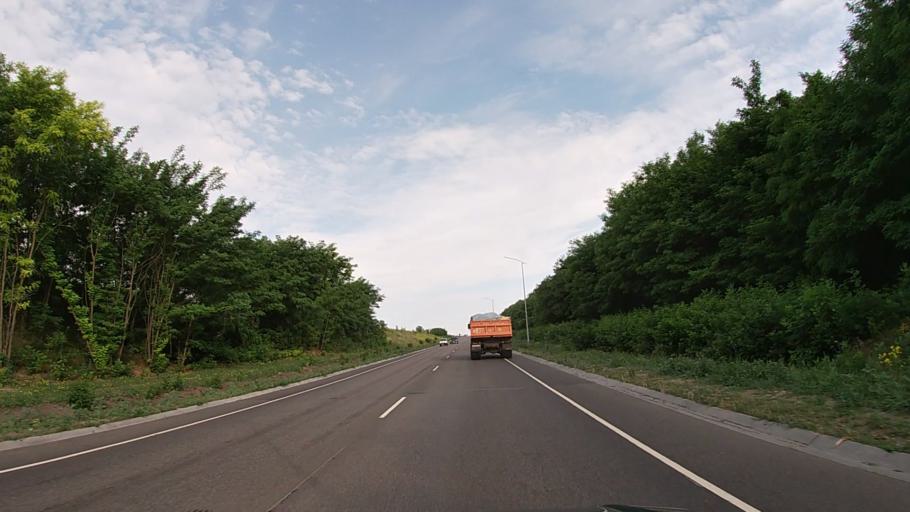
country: RU
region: Belgorod
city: Severnyy
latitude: 50.6691
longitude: 36.4885
